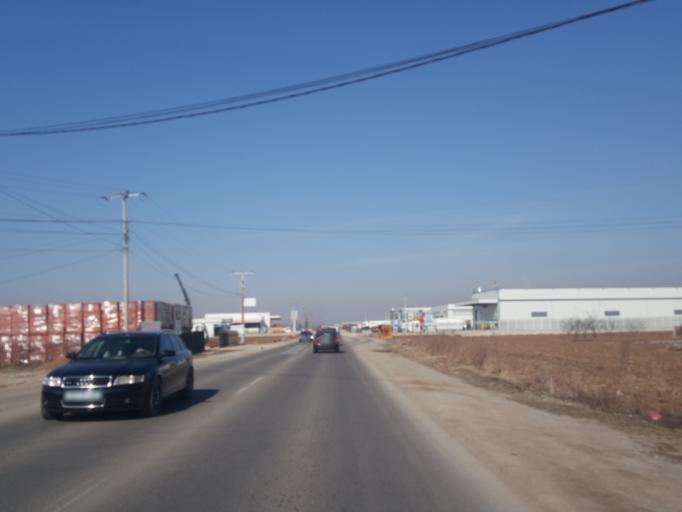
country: XK
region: Mitrovica
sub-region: Vushtrri
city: Vushtrri
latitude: 42.7822
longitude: 21.0120
